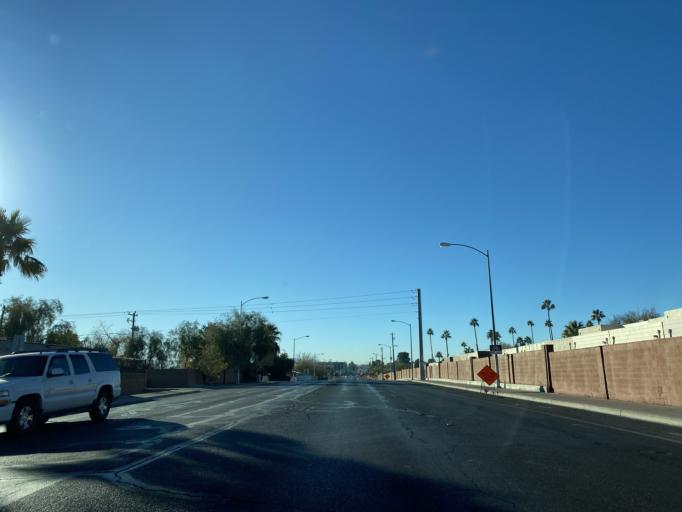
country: US
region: Nevada
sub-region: Clark County
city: Winchester
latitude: 36.1285
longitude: -115.0920
